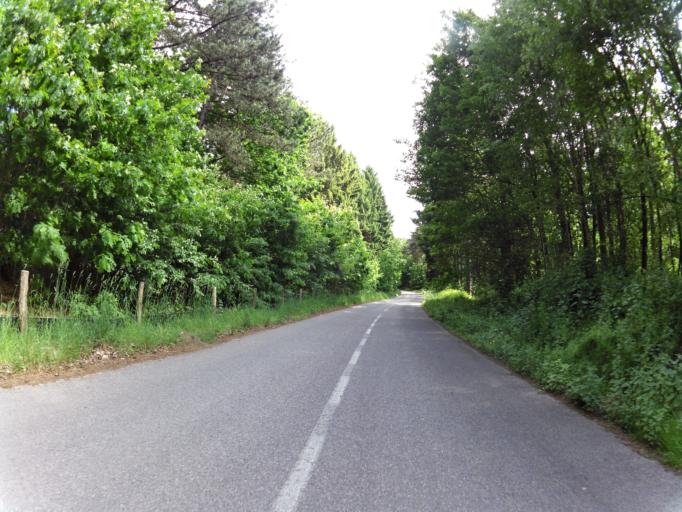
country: NL
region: Limburg
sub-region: Gemeente Brunssum
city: Brunssum
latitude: 50.9263
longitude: 6.0126
